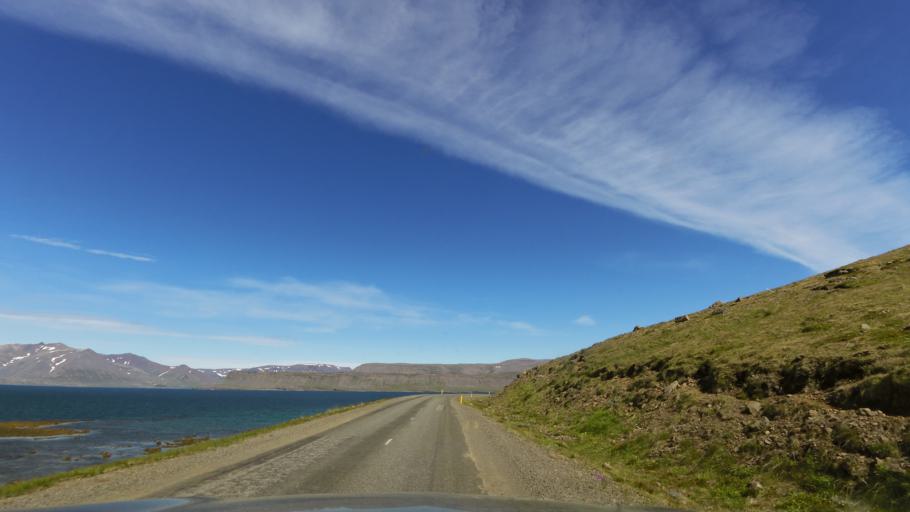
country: IS
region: Westfjords
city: Isafjoerdur
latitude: 65.6808
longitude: -23.5838
